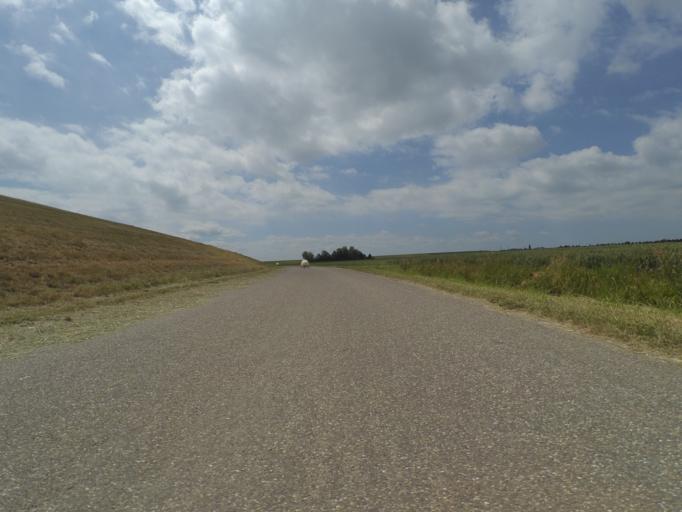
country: NL
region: Zeeland
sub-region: Gemeente Terneuzen
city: Terneuzen
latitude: 51.3948
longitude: 3.8617
